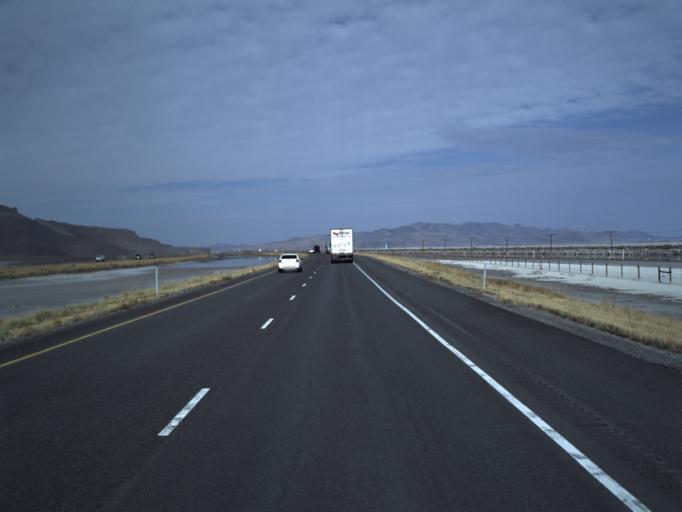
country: US
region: Utah
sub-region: Tooele County
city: Grantsville
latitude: 40.7188
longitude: -112.5504
